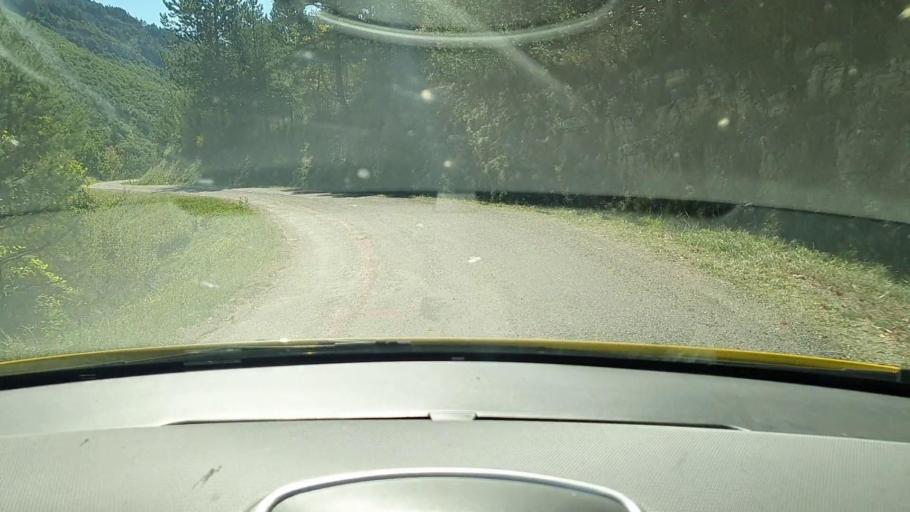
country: FR
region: Languedoc-Roussillon
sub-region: Departement du Gard
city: Aveze
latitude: 43.9611
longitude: 3.4355
